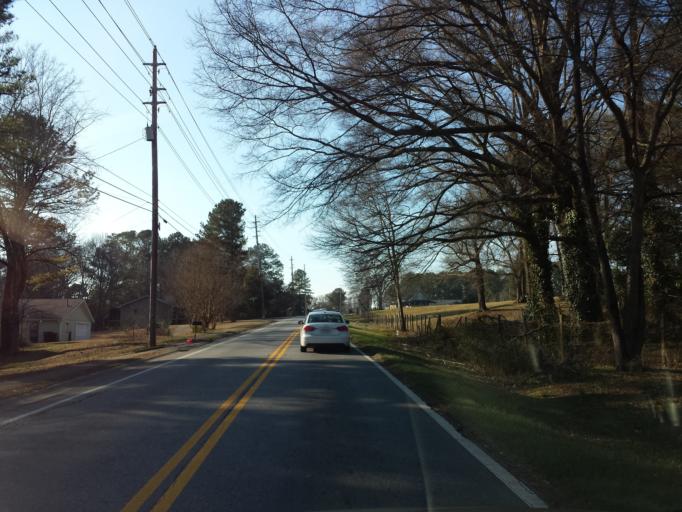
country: US
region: Georgia
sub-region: Cherokee County
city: Woodstock
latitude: 34.0533
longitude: -84.5109
